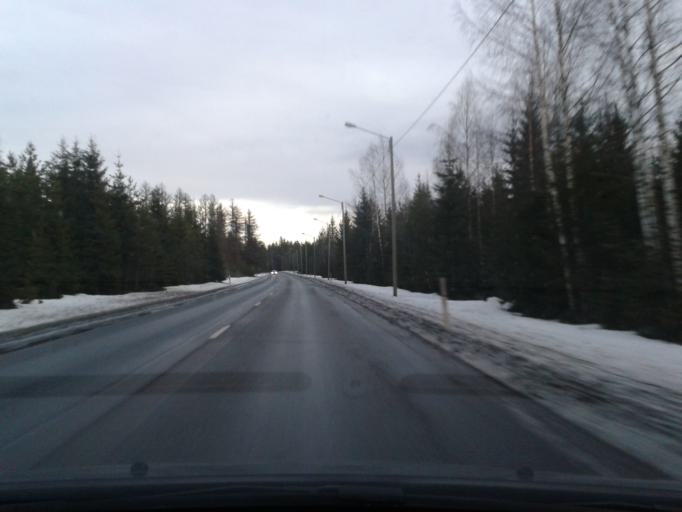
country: SE
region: Vaesternorrland
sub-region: Solleftea Kommun
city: Solleftea
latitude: 63.1510
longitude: 17.3368
